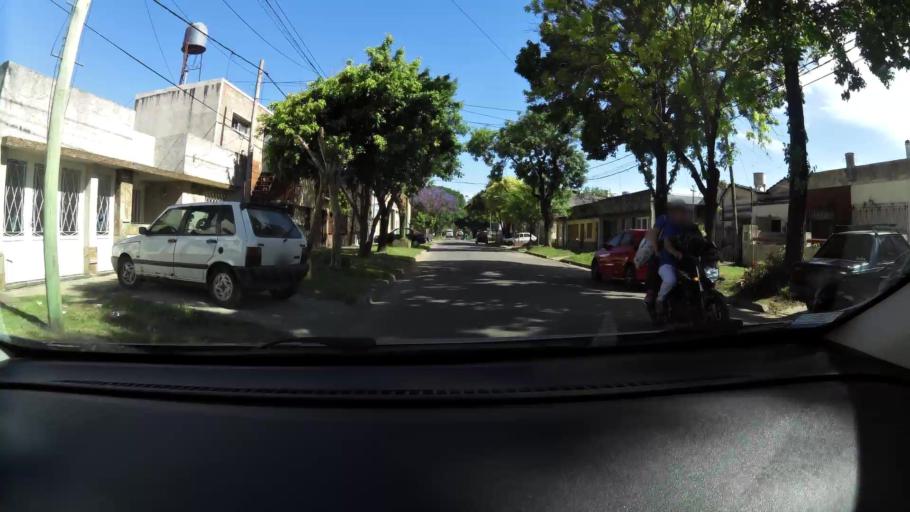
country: AR
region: Santa Fe
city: Granadero Baigorria
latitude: -32.9339
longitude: -60.7189
